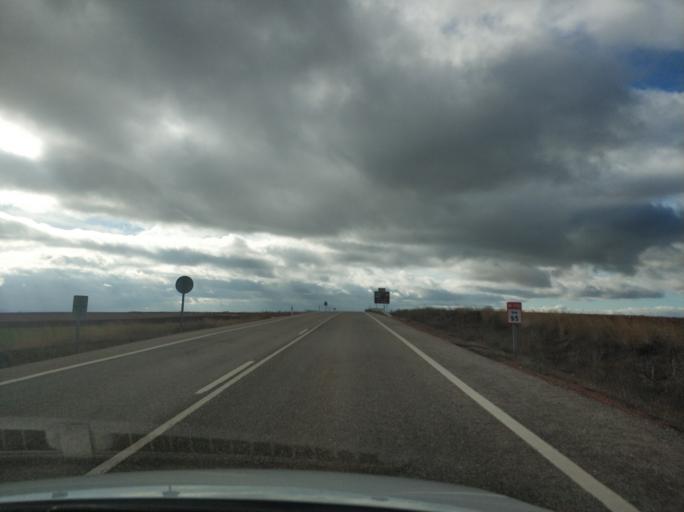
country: ES
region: Castille and Leon
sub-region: Provincia de Segovia
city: Ayllon
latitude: 41.4330
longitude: -3.3652
